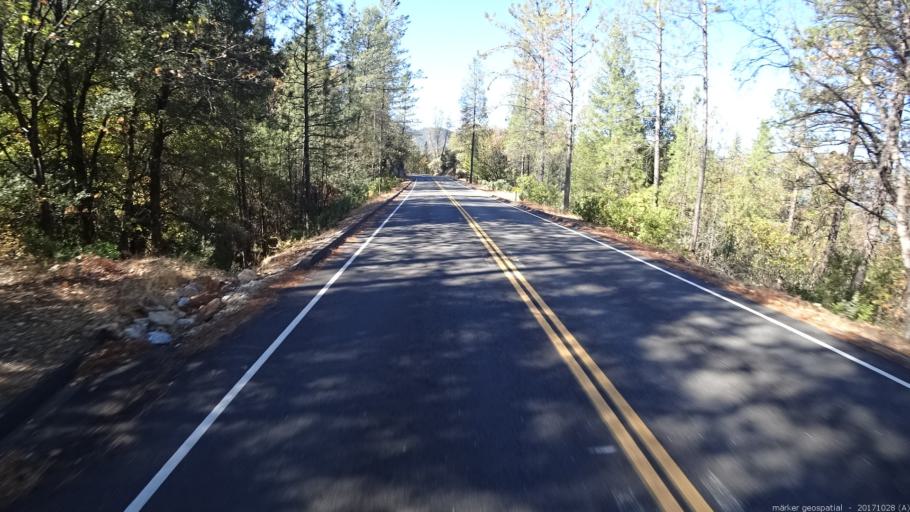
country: US
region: California
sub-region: Shasta County
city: Shasta
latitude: 40.6155
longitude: -122.5663
